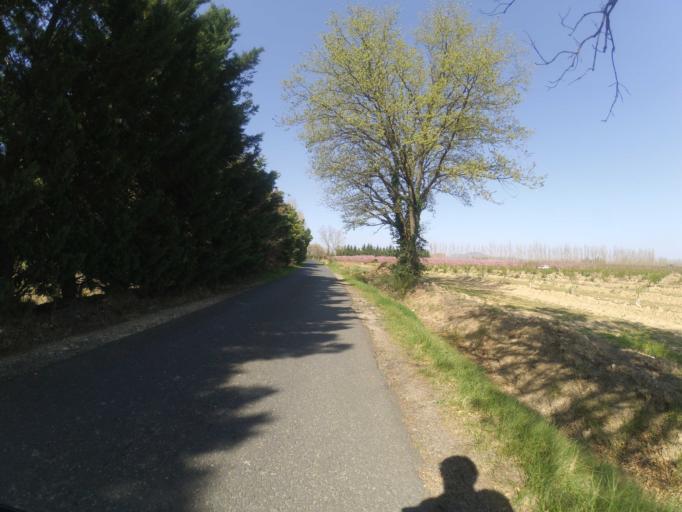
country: FR
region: Languedoc-Roussillon
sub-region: Departement des Pyrenees-Orientales
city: Thuir
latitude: 42.6532
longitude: 2.7645
